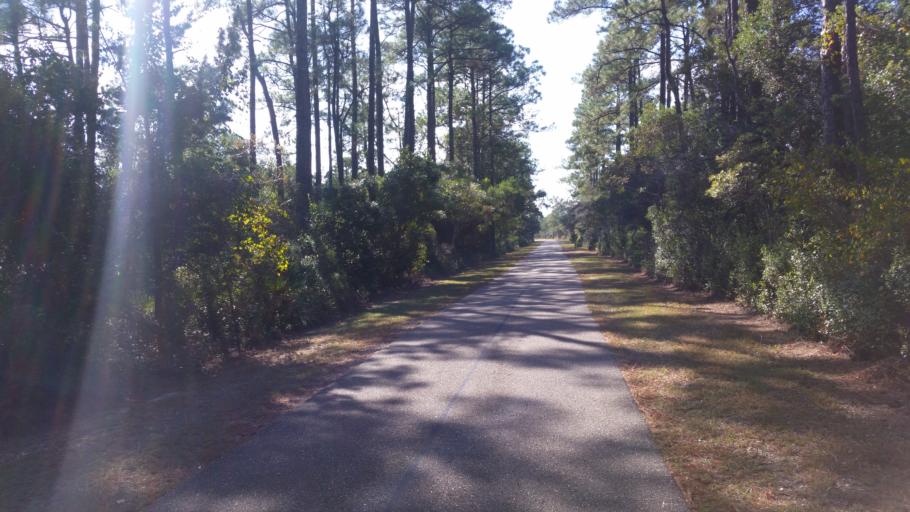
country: US
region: Alabama
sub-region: Baldwin County
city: Orange Beach
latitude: 30.2761
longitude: -87.5976
